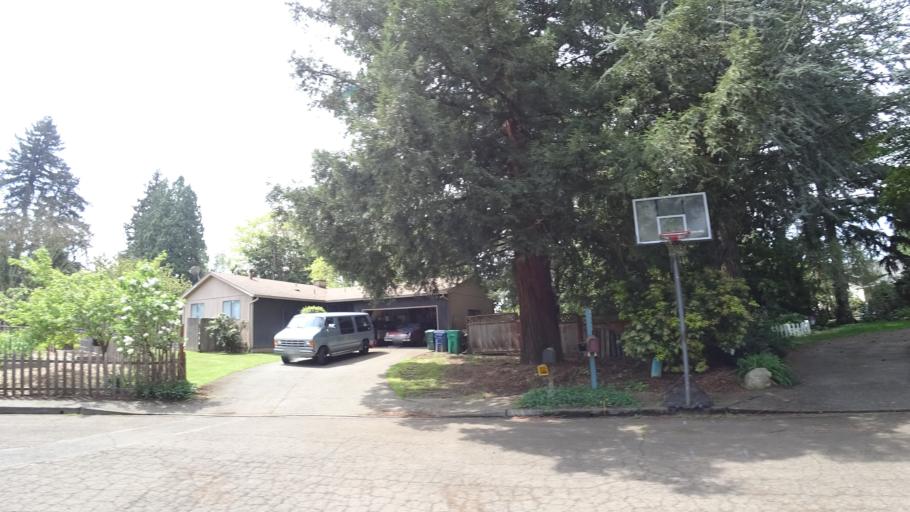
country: US
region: Oregon
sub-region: Clackamas County
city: Milwaukie
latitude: 45.4489
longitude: -122.6107
